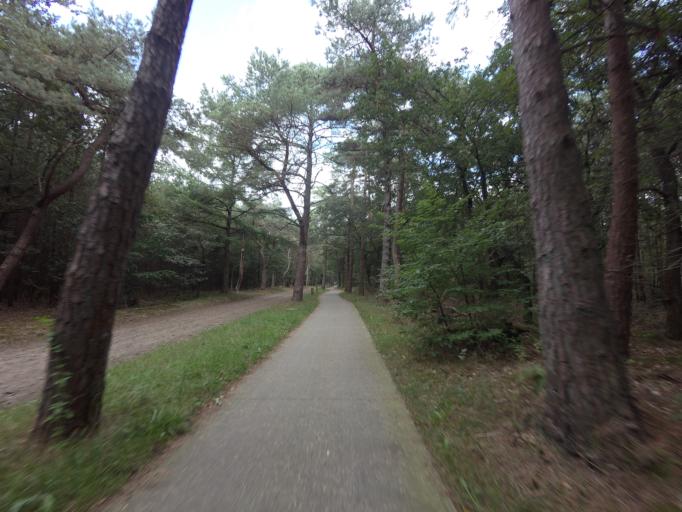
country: NL
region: Drenthe
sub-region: Gemeente Westerveld
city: Dwingeloo
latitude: 52.8151
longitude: 6.3595
